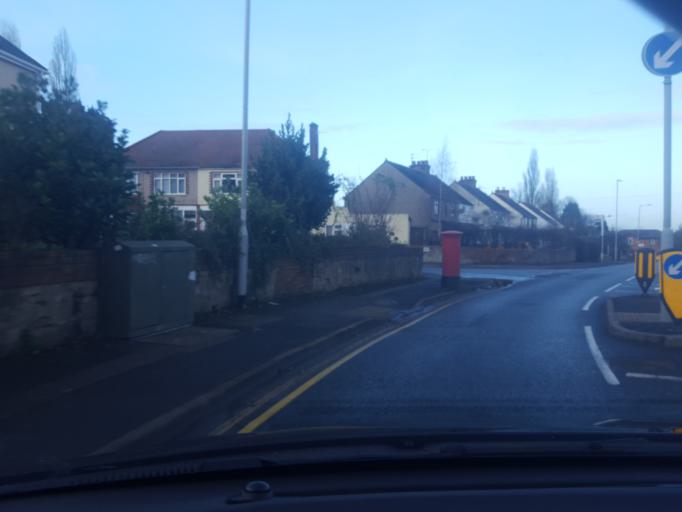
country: GB
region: England
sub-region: Wolverhampton
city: Wolverhampton
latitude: 52.6091
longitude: -2.1512
